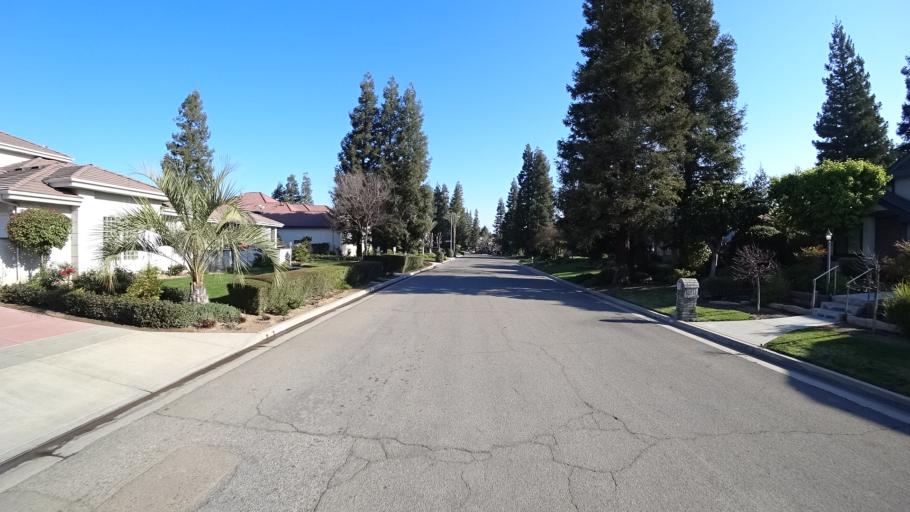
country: US
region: California
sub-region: Fresno County
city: Clovis
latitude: 36.8654
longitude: -119.7956
